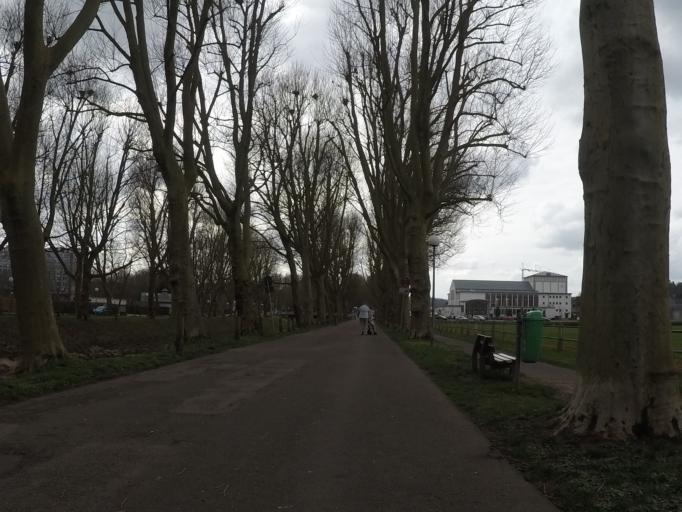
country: DE
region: Rheinland-Pfalz
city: Zweibrucken
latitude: 49.2526
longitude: 7.3723
